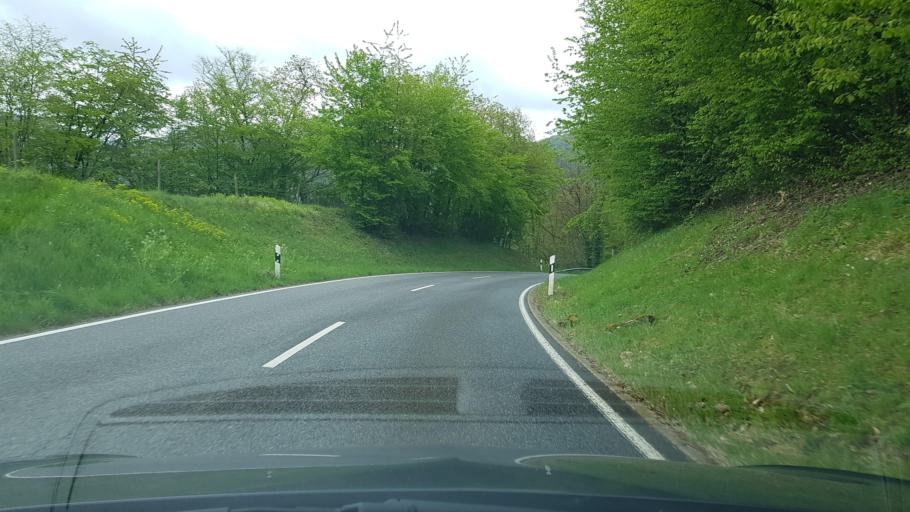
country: DE
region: Rheinland-Pfalz
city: Oberfell
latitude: 50.2500
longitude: 7.4367
